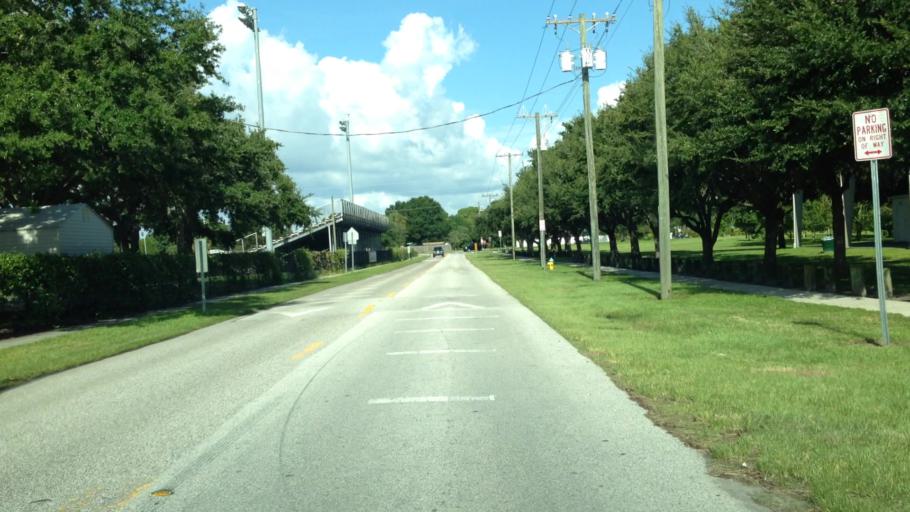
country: US
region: Florida
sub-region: Hillsborough County
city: Tampa
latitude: 27.8755
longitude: -82.5164
